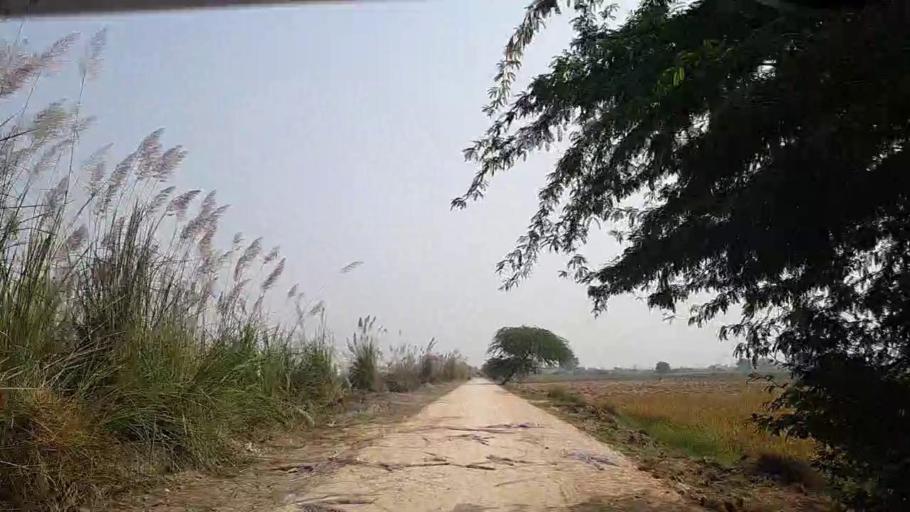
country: PK
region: Sindh
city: Garhi Yasin
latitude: 27.9212
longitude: 68.5761
